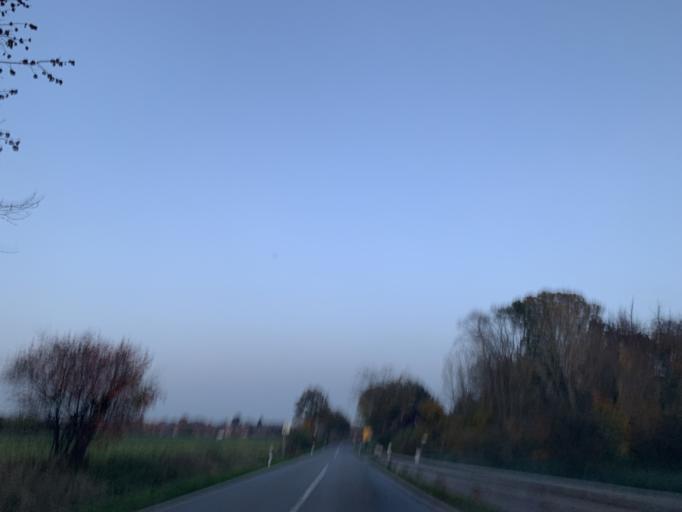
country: DE
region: North Rhine-Westphalia
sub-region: Regierungsbezirk Munster
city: Havixbeck
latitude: 51.9633
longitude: 7.4170
